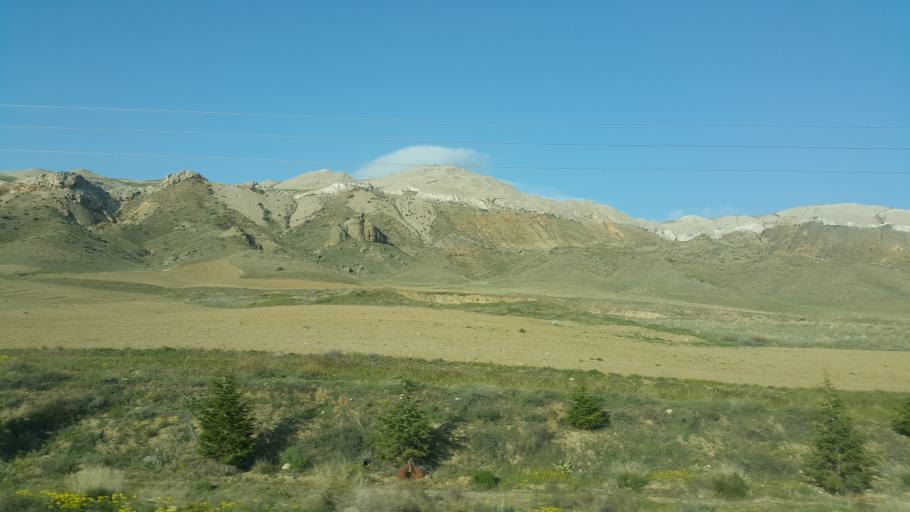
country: TR
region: Ankara
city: Sereflikochisar
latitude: 38.9978
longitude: 33.4668
